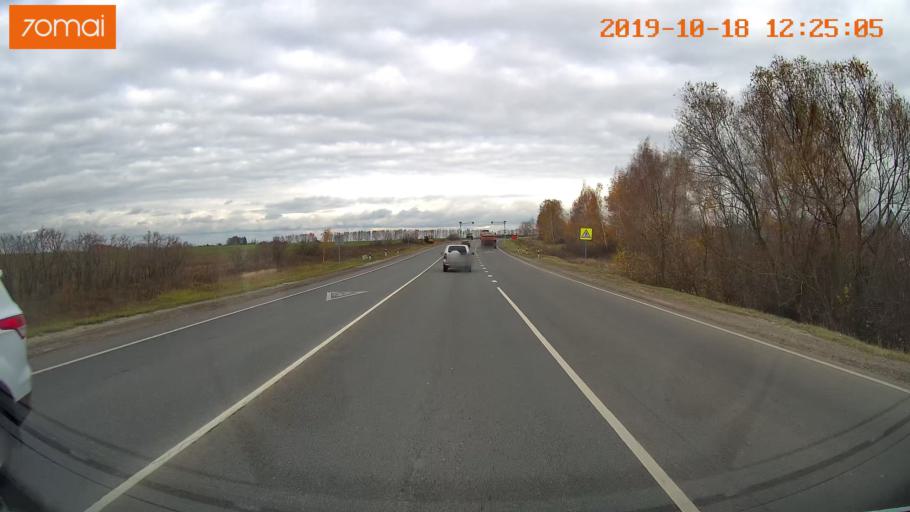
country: RU
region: Rjazan
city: Rybnoye
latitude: 54.5454
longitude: 39.5168
